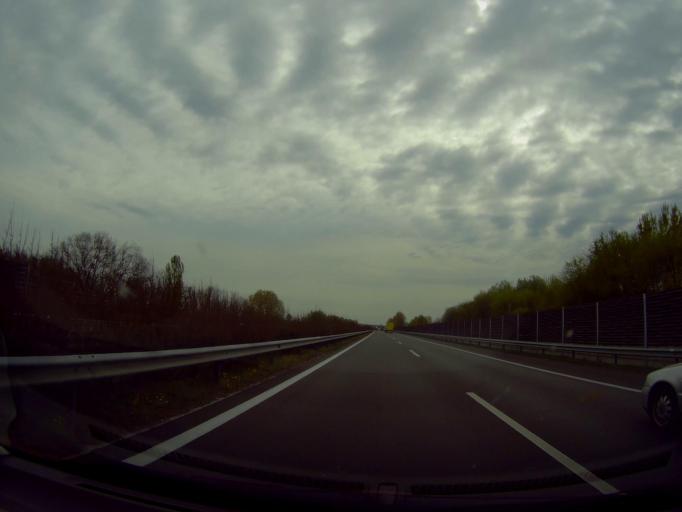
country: HU
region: Csongrad
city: Szatymaz
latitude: 46.3364
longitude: 20.0204
